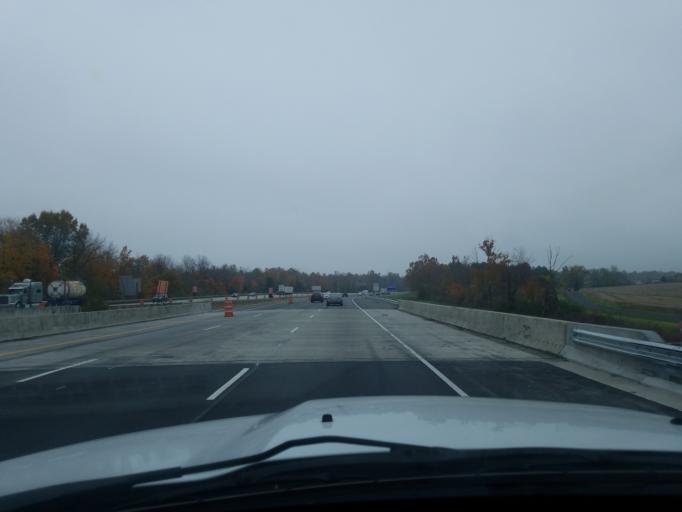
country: US
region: Kentucky
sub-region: Hardin County
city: Elizabethtown
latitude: 37.6869
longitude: -85.8421
